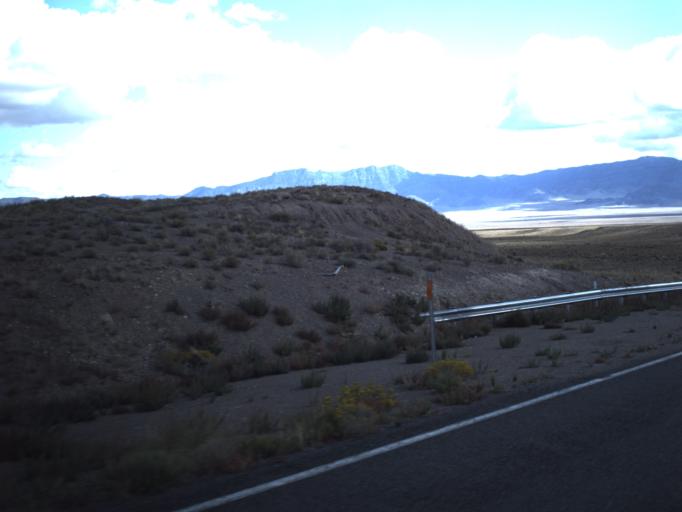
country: US
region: Utah
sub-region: Beaver County
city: Milford
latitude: 38.5685
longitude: -113.7799
